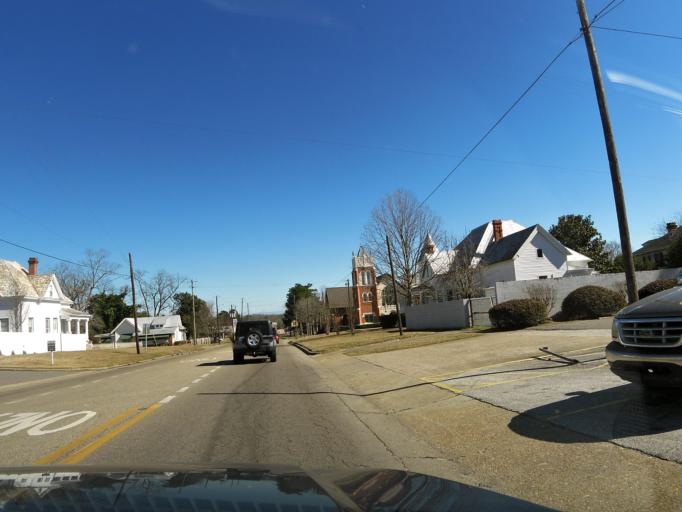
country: US
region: Alabama
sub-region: Bullock County
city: Union Springs
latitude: 32.1433
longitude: -85.7157
